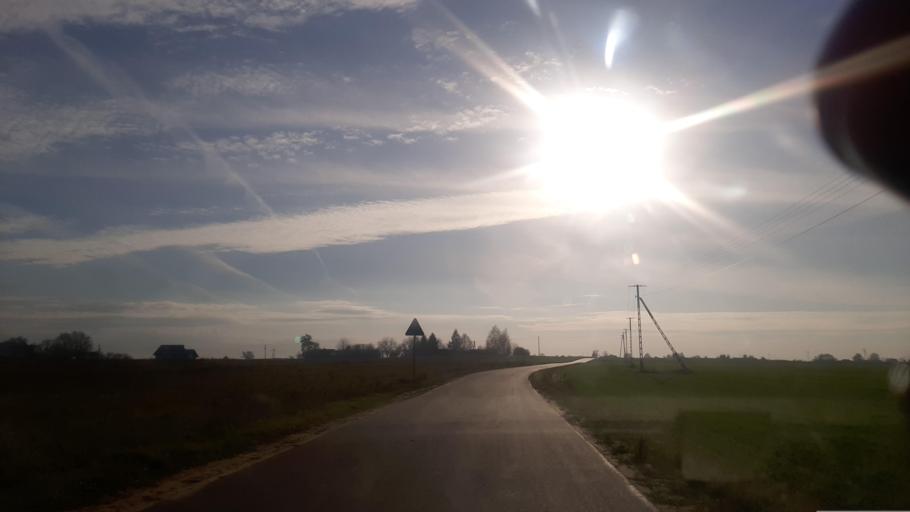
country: PL
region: Lublin Voivodeship
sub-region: Powiat lubelski
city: Garbow
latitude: 51.3949
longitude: 22.3504
